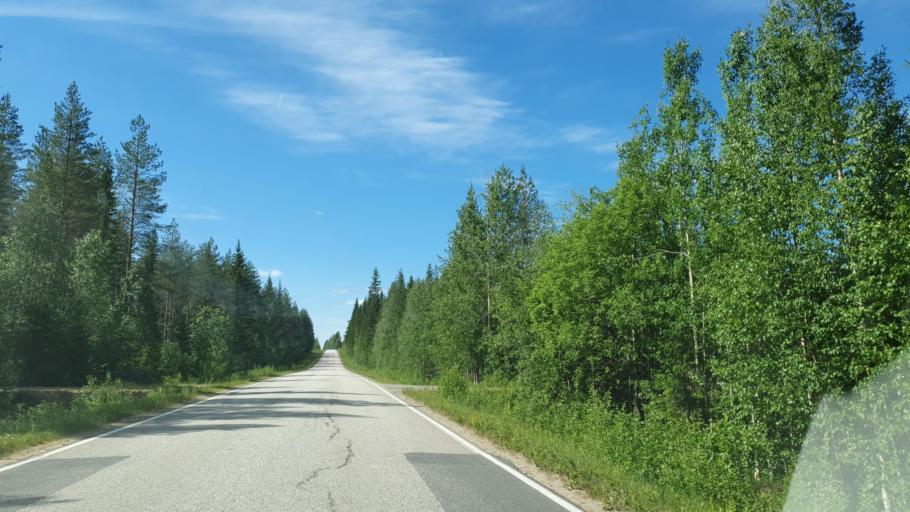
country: FI
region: Kainuu
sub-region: Kehys-Kainuu
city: Suomussalmi
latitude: 64.5903
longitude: 29.0769
